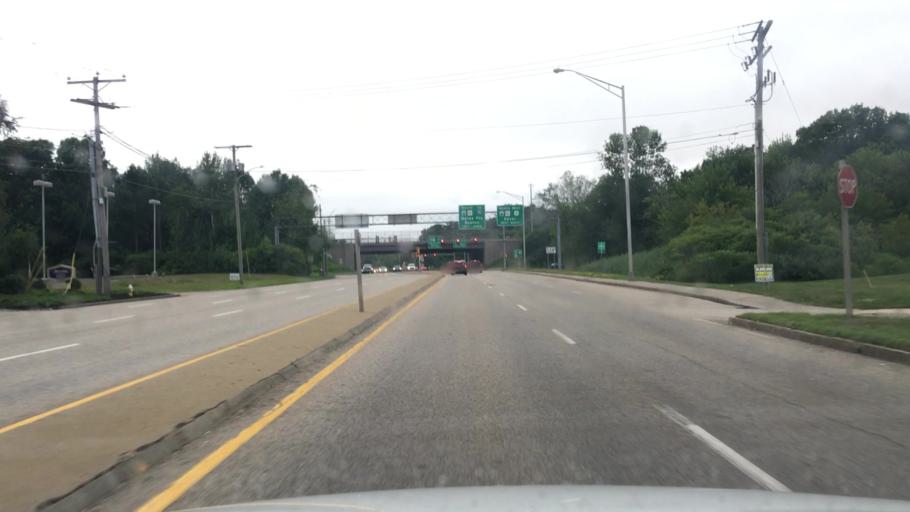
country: US
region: Maine
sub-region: York County
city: South Eliot
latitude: 43.0919
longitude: -70.7999
